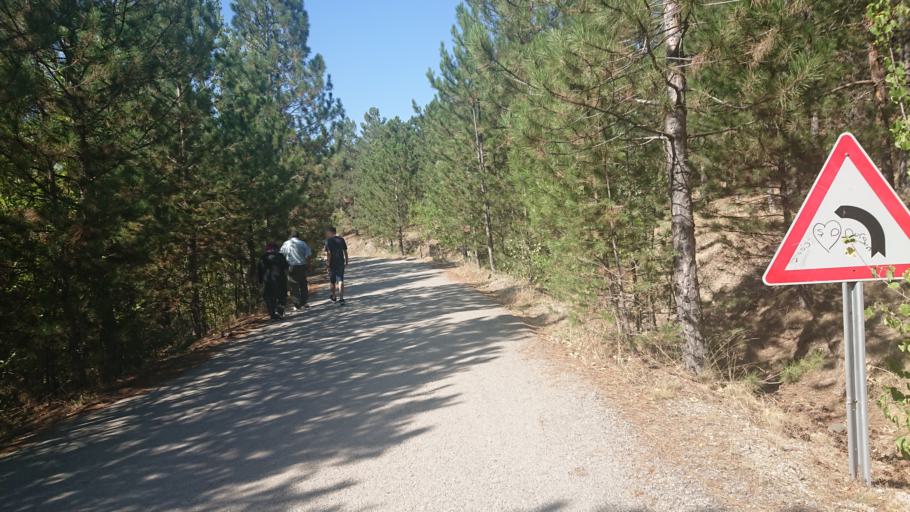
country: TR
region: Ankara
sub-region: Goelbasi
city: Golbasi
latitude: 39.8177
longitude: 32.8212
